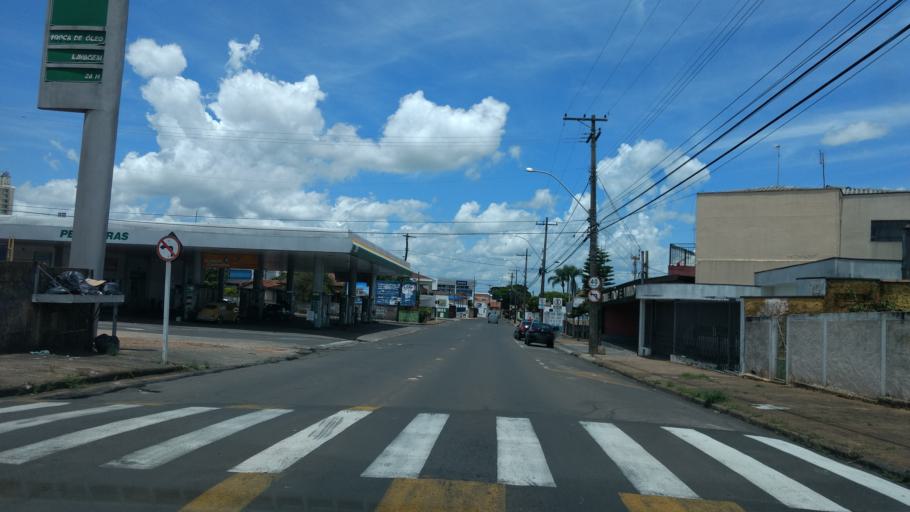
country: BR
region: Sao Paulo
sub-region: Botucatu
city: Botucatu
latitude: -22.8705
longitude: -48.4539
